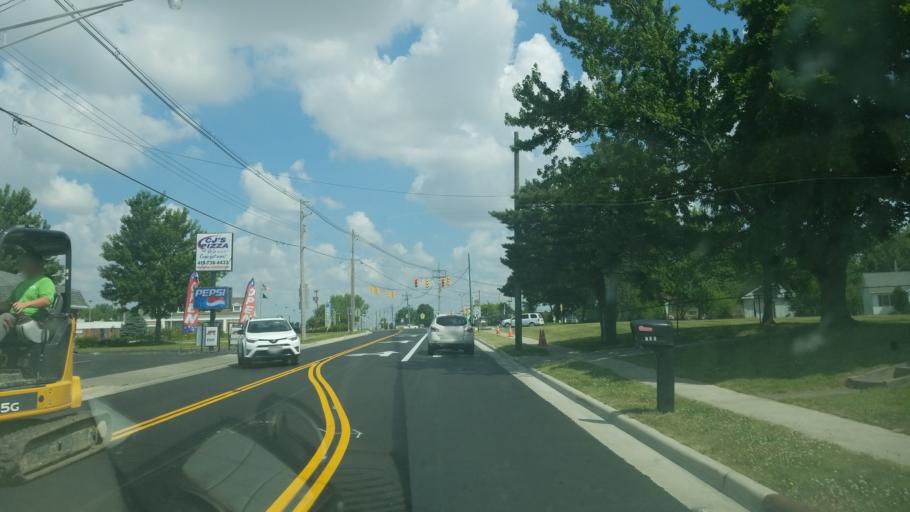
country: US
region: Ohio
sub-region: Auglaize County
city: Wapakoneta
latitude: 40.5785
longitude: -84.2023
